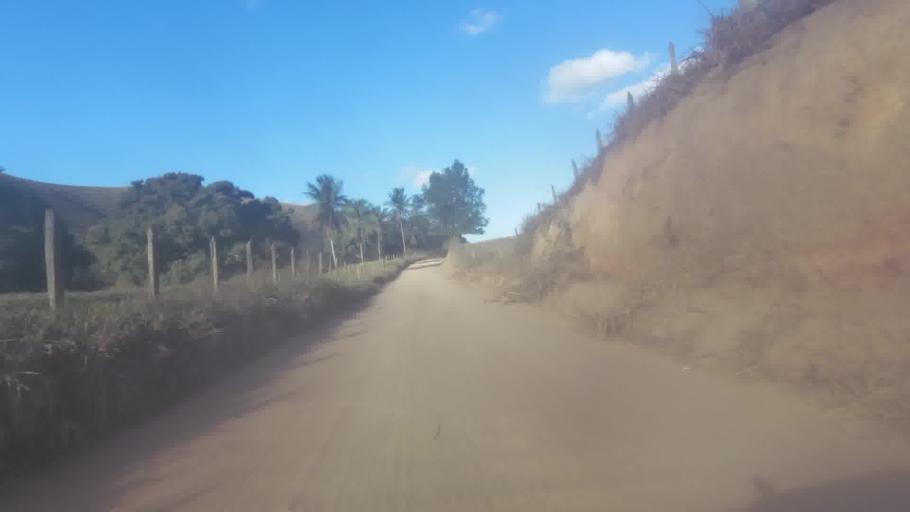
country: BR
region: Espirito Santo
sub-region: Mimoso Do Sul
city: Mimoso do Sul
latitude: -21.1024
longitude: -41.1325
